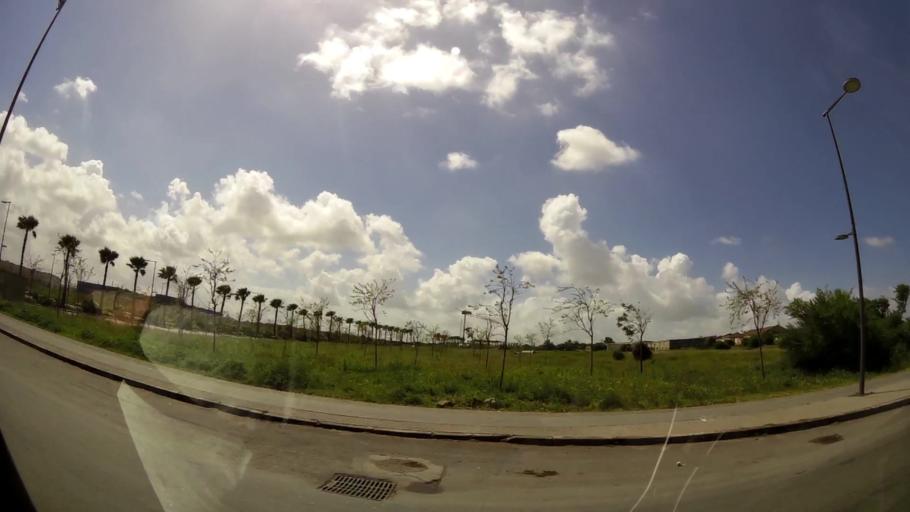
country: MA
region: Grand Casablanca
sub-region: Mediouna
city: Tit Mellil
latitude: 33.6337
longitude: -7.4629
